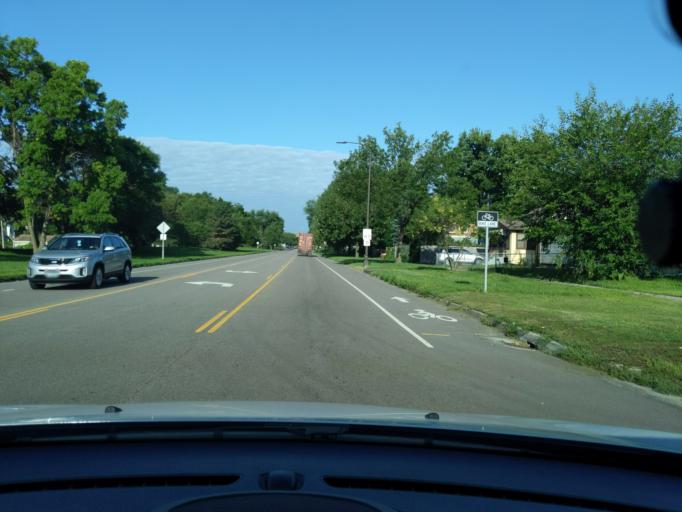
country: US
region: Minnesota
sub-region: Ramsey County
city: Saint Paul
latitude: 44.9648
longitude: -93.1315
